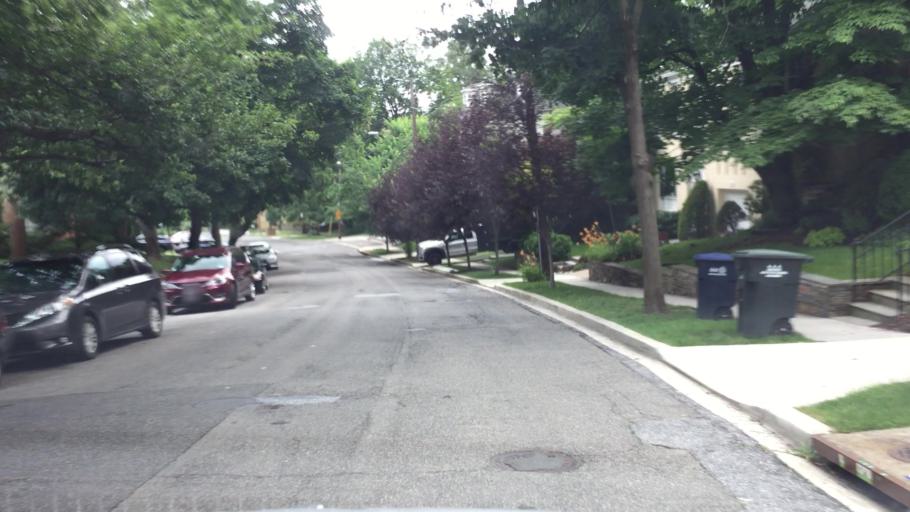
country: US
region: Washington, D.C.
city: Washington, D.C.
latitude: 38.9266
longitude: -77.0592
